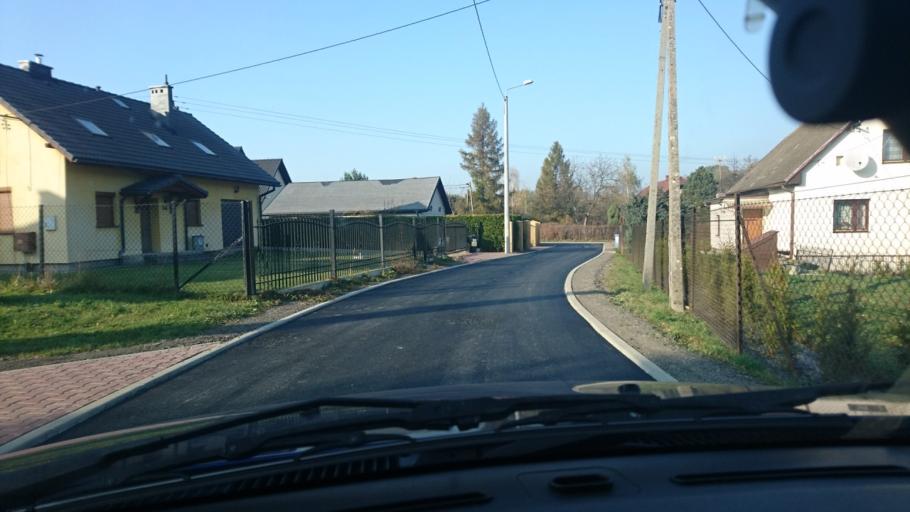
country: PL
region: Silesian Voivodeship
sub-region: Bielsko-Biala
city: Bielsko-Biala
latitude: 49.8485
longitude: 19.0686
